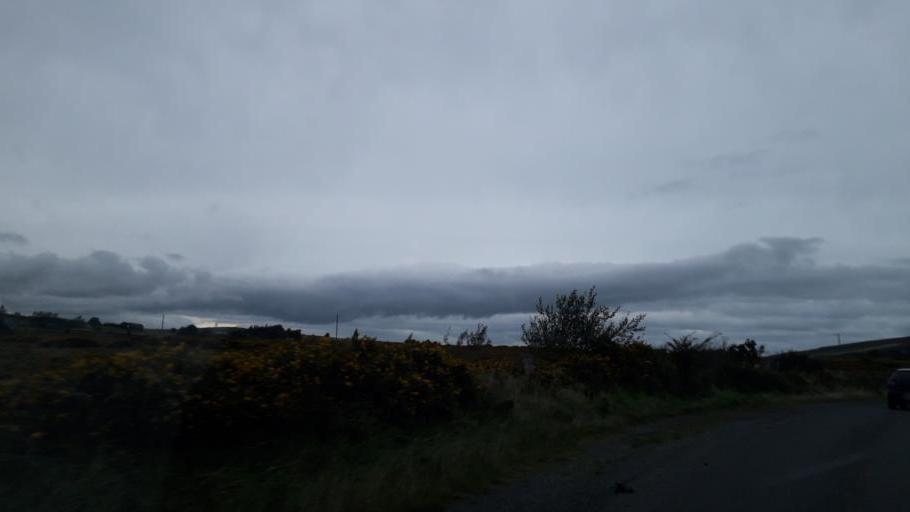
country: IE
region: Leinster
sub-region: Wicklow
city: Kilmacanoge
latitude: 53.1368
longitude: -6.1754
